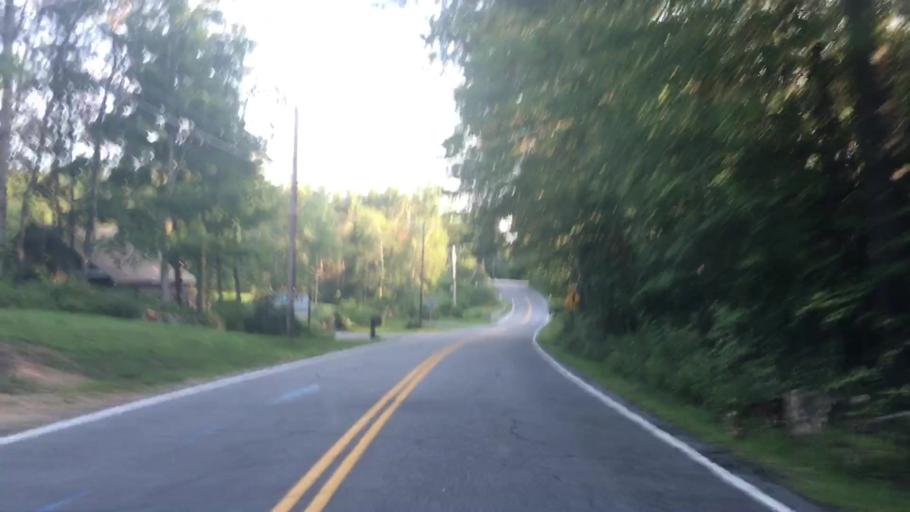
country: US
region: New Hampshire
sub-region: Belknap County
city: Gilmanton
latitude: 43.4816
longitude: -71.4297
